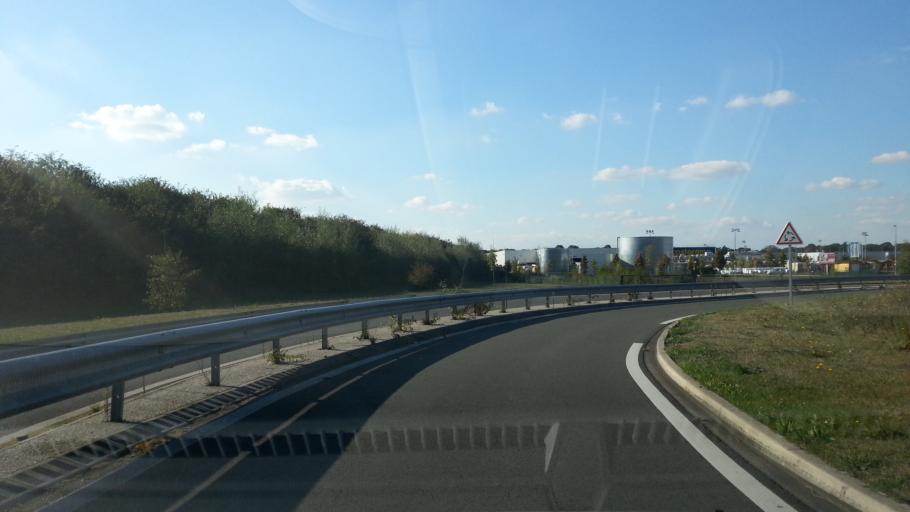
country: FR
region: Picardie
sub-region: Departement de l'Oise
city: Saint-Maximin
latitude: 49.2286
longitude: 2.4683
